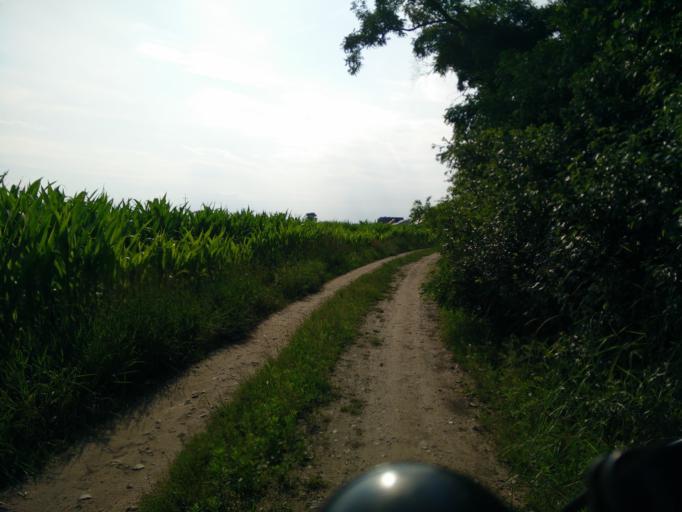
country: PL
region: Greater Poland Voivodeship
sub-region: Powiat sredzki
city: Sroda Wielkopolska
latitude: 52.2616
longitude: 17.3113
